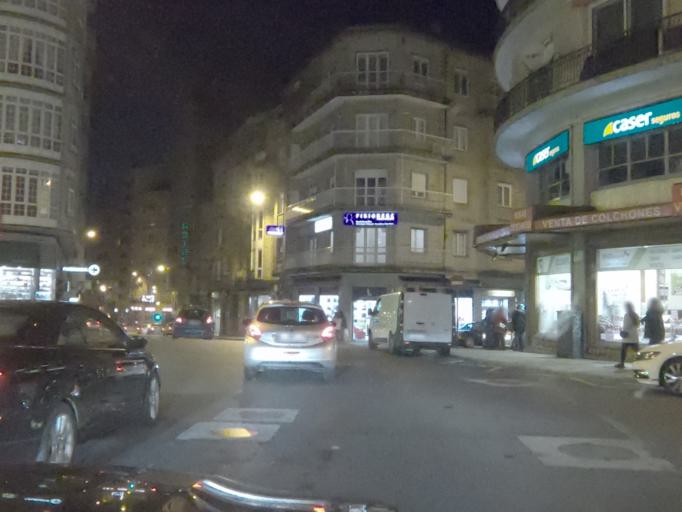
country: ES
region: Galicia
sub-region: Provincia de Ourense
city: Ourense
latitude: 42.3423
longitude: -7.8622
